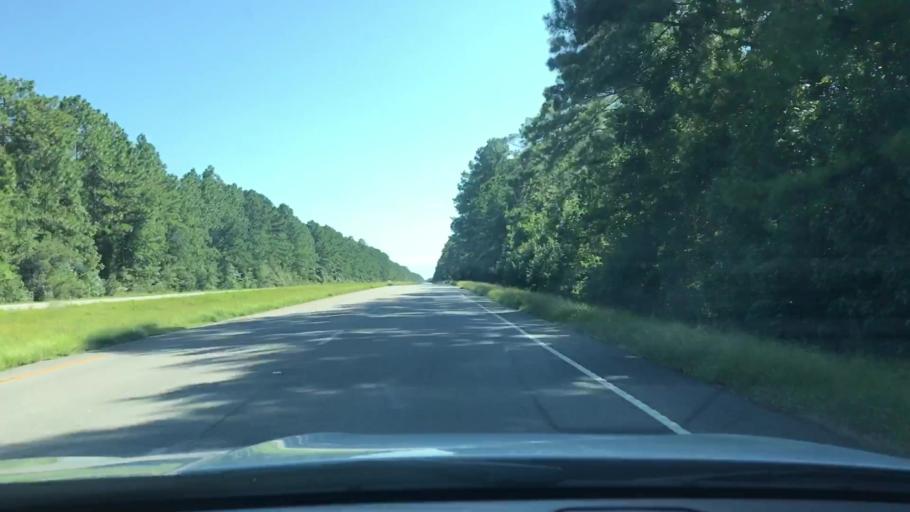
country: US
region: South Carolina
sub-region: Charleston County
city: Awendaw
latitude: 33.1659
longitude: -79.4228
